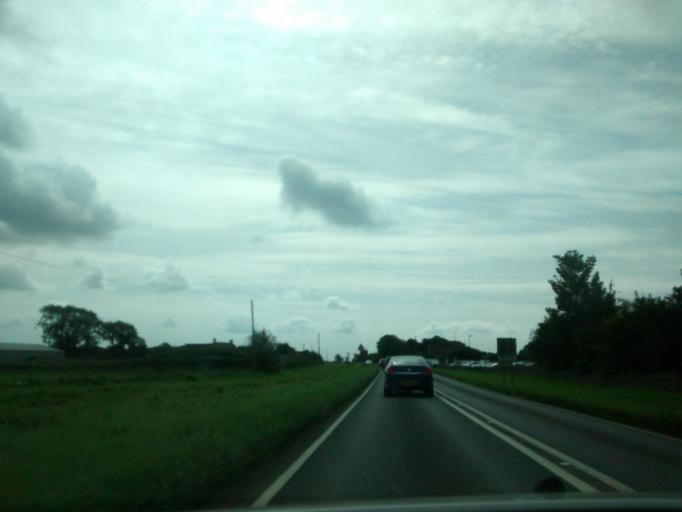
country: GB
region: England
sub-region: South Gloucestershire
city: Cold Ashton
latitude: 51.4186
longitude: -2.3970
